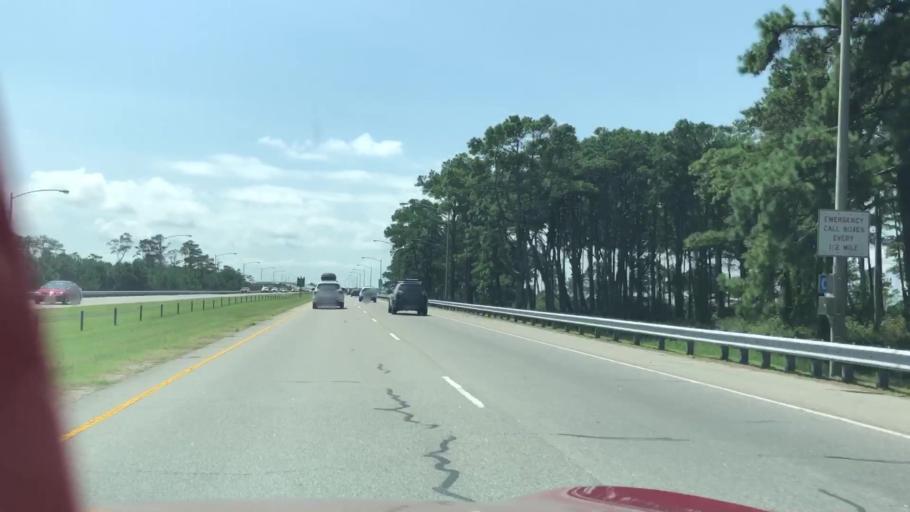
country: US
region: Virginia
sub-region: Northampton County
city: Cape Charles
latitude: 37.1268
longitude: -75.9679
